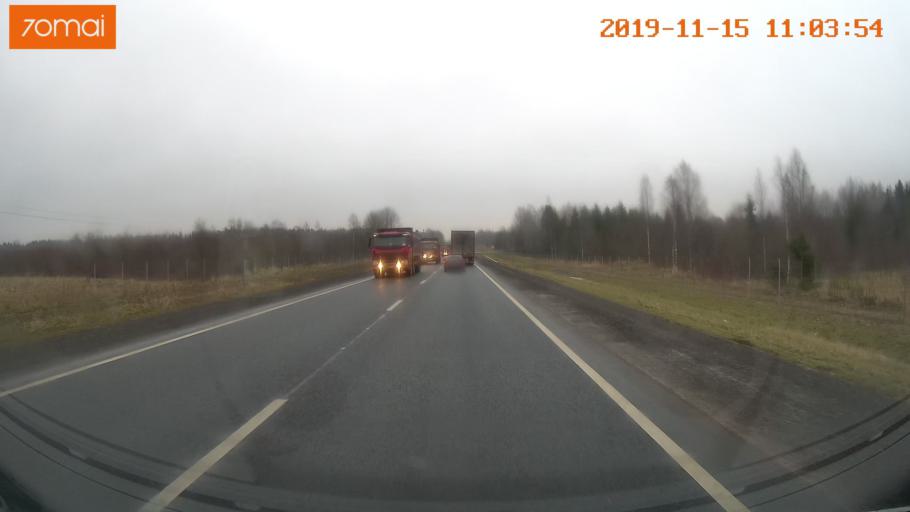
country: RU
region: Vologda
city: Chebsara
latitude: 59.1224
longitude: 38.9724
